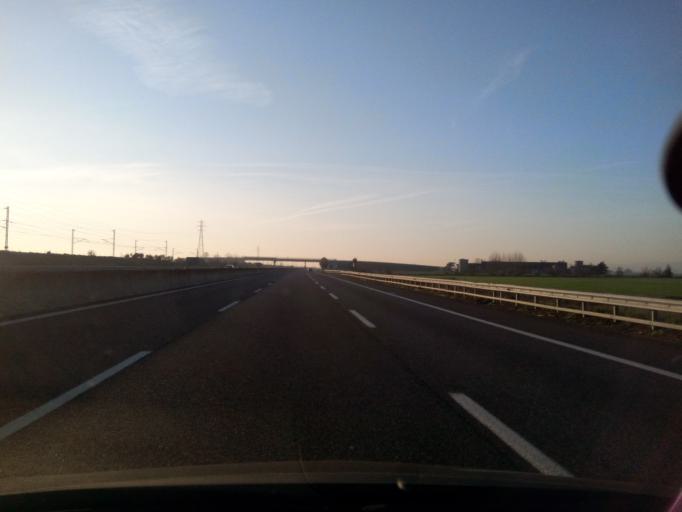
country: IT
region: Lombardy
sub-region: Provincia di Lodi
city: Senna Lodigiana
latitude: 45.1675
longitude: 9.5988
